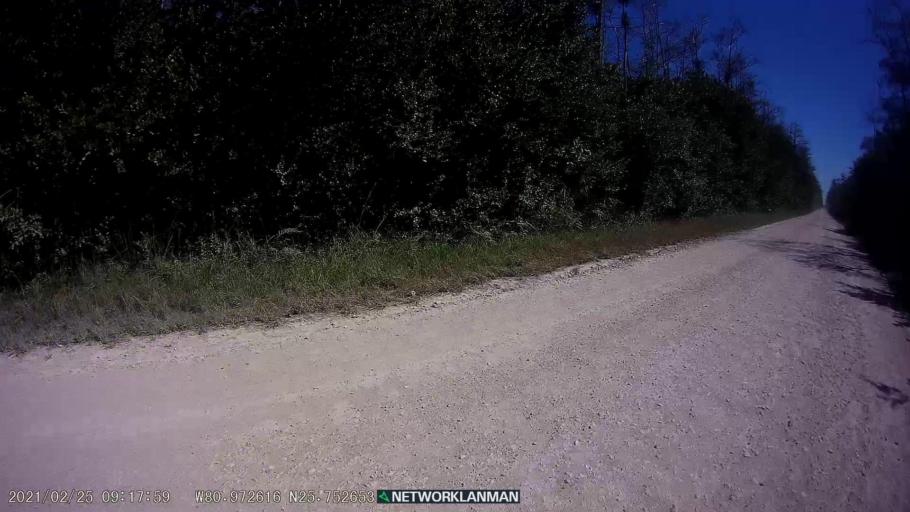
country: US
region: Florida
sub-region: Miami-Dade County
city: The Hammocks
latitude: 25.7526
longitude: -80.9726
